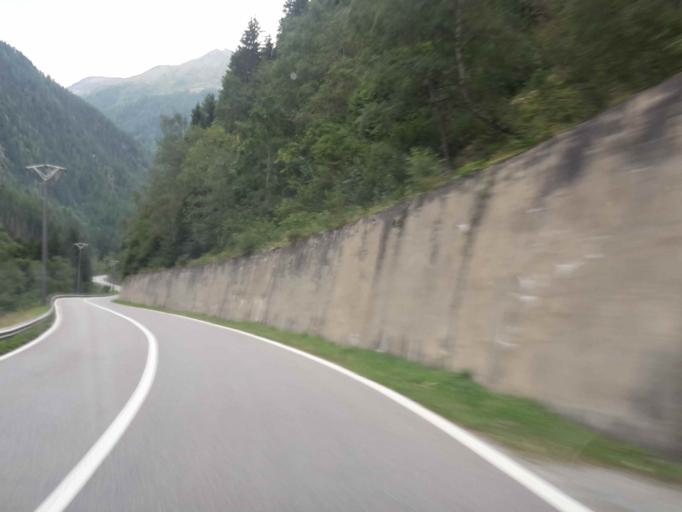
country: CH
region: Valais
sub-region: Saint-Maurice District
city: Salvan
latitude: 46.0703
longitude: 6.9781
